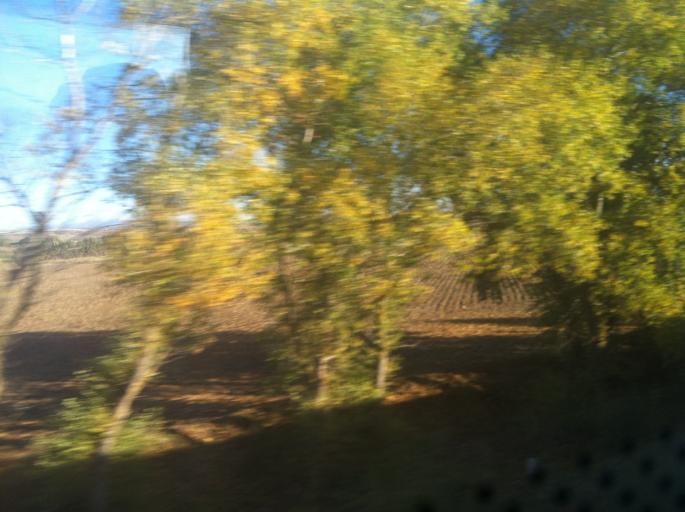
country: ES
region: Castille and Leon
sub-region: Provincia de Palencia
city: Torquemada
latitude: 42.0096
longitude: -4.3358
